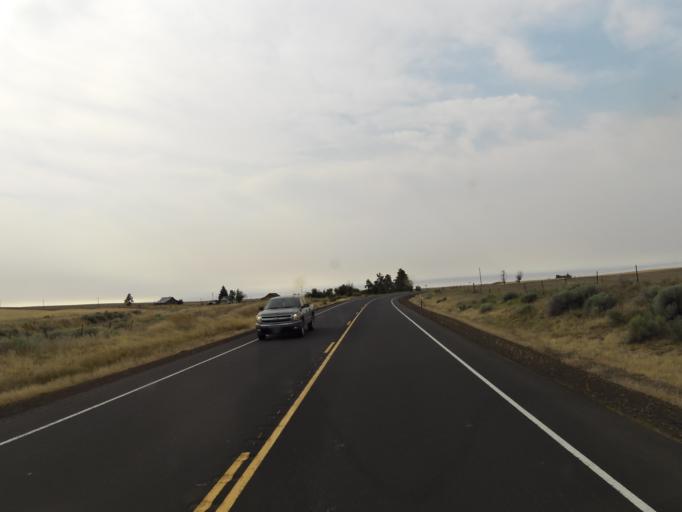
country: US
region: Oregon
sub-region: Sherman County
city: Moro
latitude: 45.3332
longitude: -120.7698
